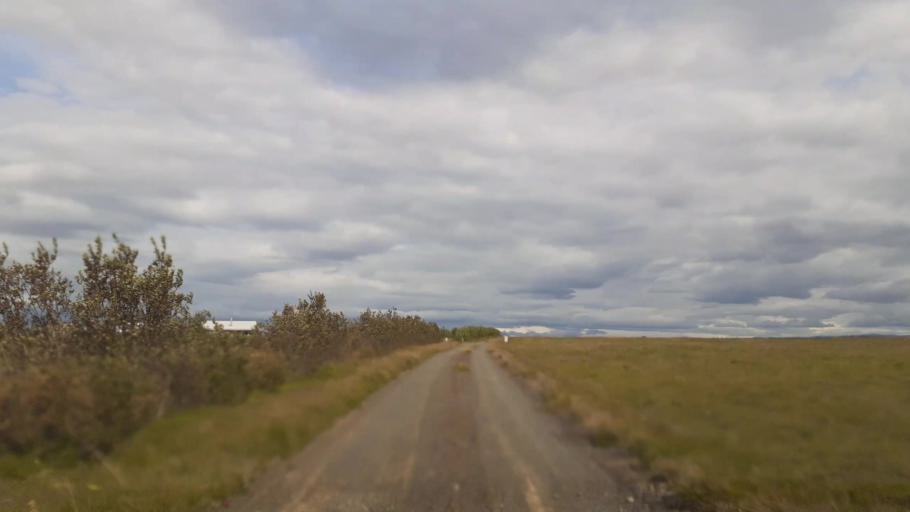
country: IS
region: South
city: Vestmannaeyjar
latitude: 63.7722
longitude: -20.2983
